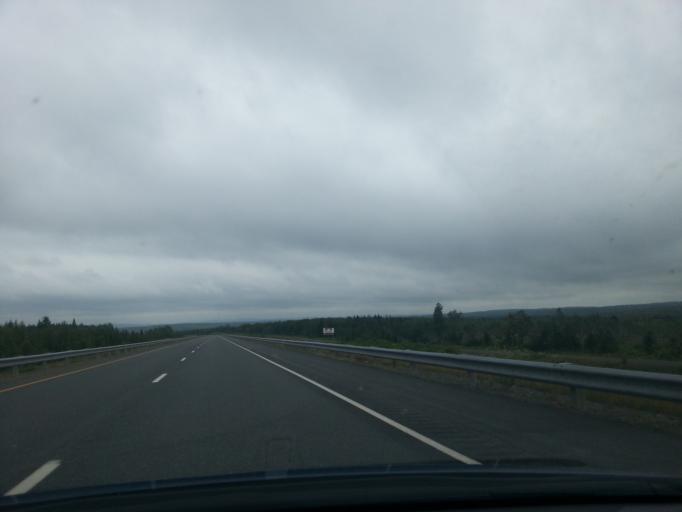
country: CA
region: New Brunswick
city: Nackawic
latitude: 45.8941
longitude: -67.0661
